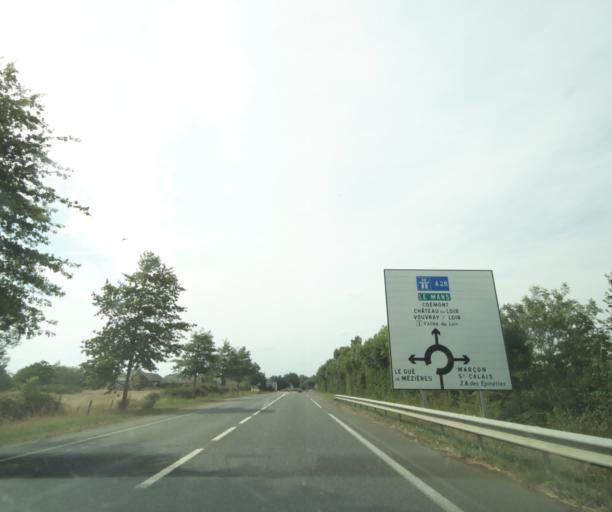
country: FR
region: Pays de la Loire
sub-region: Departement de la Sarthe
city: Chateau-du-Loir
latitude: 47.6756
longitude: 0.4527
